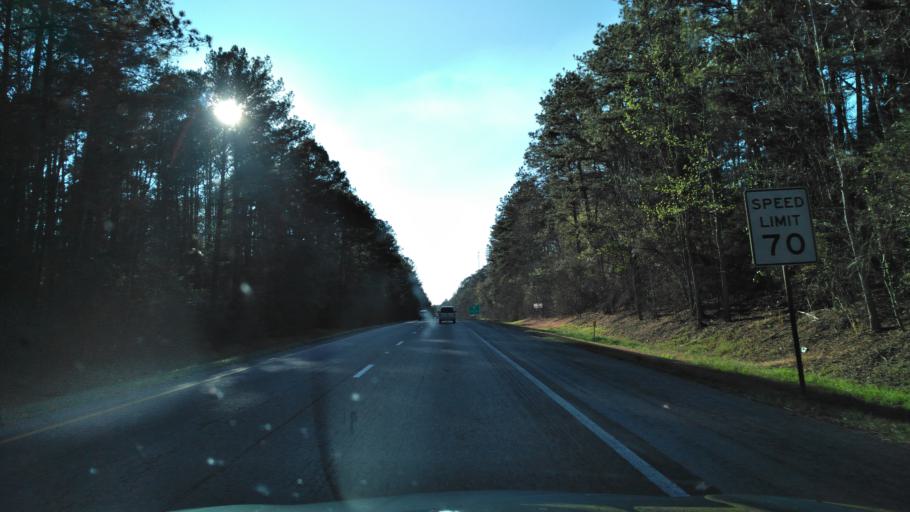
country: US
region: Alabama
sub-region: Baldwin County
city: Bay Minette
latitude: 30.9527
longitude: -87.8338
